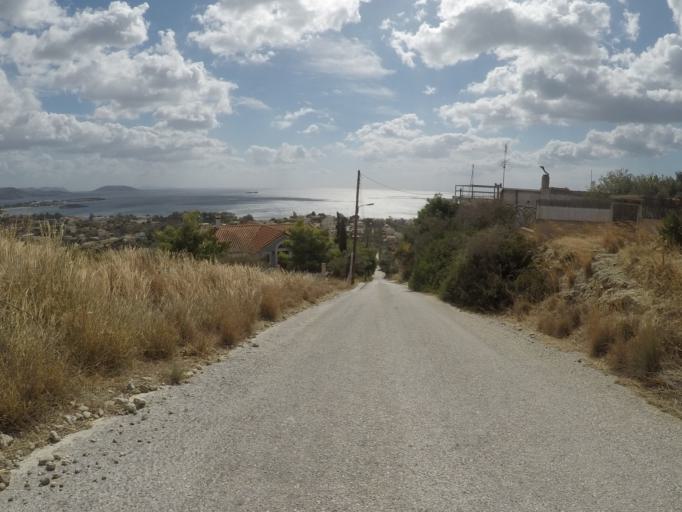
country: GR
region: Attica
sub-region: Nomarchia Anatolikis Attikis
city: Agios Dimitrios Kropias
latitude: 37.7990
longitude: 23.8781
